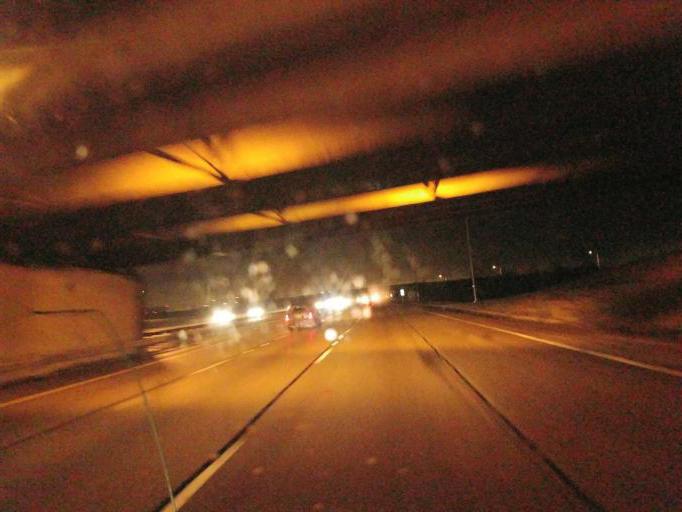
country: US
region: Illinois
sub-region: Saint Clair County
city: Caseyville
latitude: 38.6730
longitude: -90.0296
